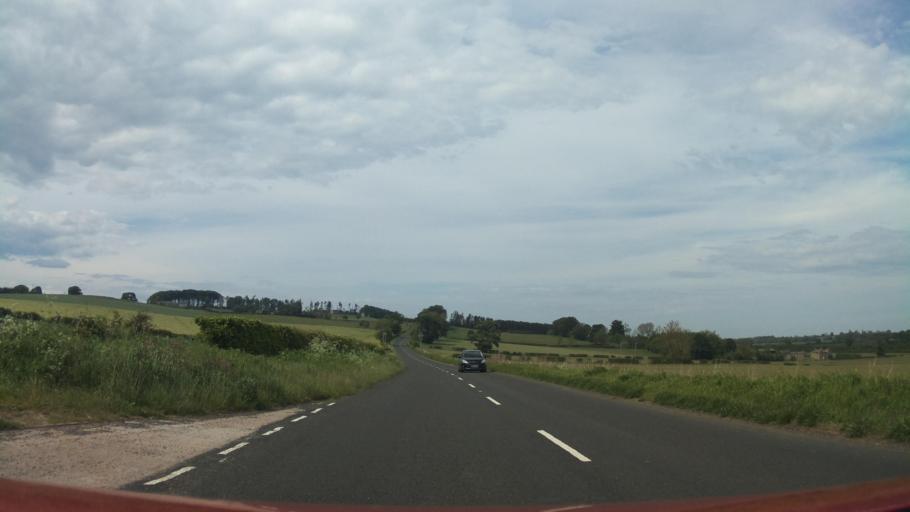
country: GB
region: England
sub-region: Northumberland
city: Alnwick
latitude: 55.4441
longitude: -1.7101
